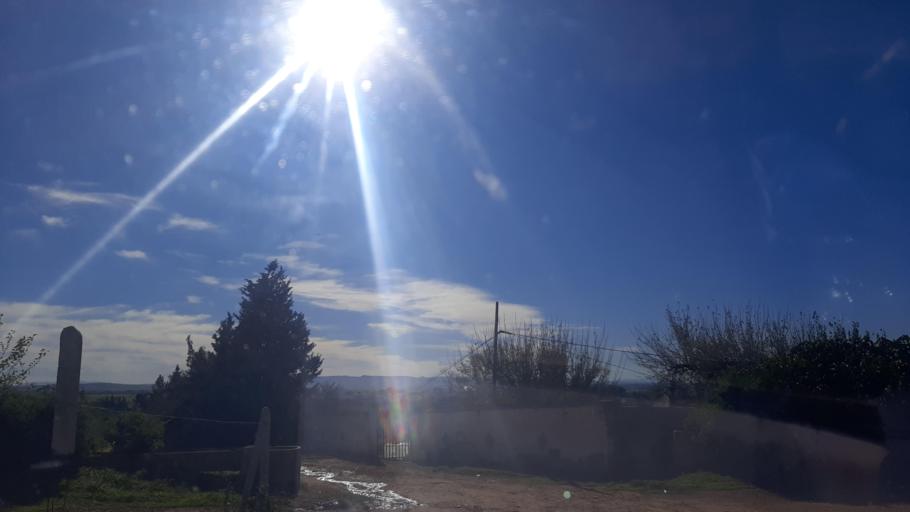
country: TN
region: Tunis
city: Oued Lill
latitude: 36.7616
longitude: 9.9821
